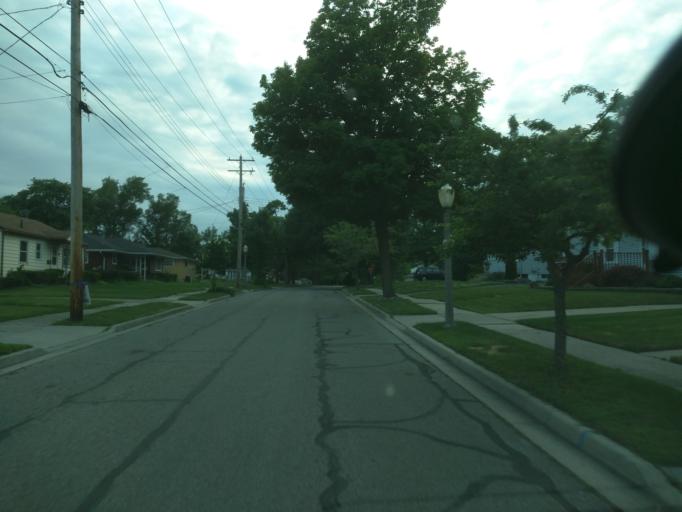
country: US
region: Michigan
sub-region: Ingham County
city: Lansing
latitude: 42.7052
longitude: -84.5789
